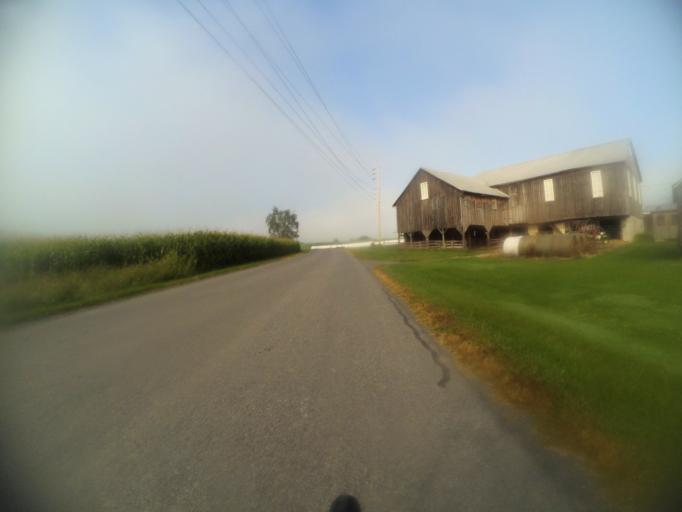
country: US
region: Pennsylvania
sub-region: Centre County
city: Centre Hall
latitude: 40.8499
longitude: -77.6619
